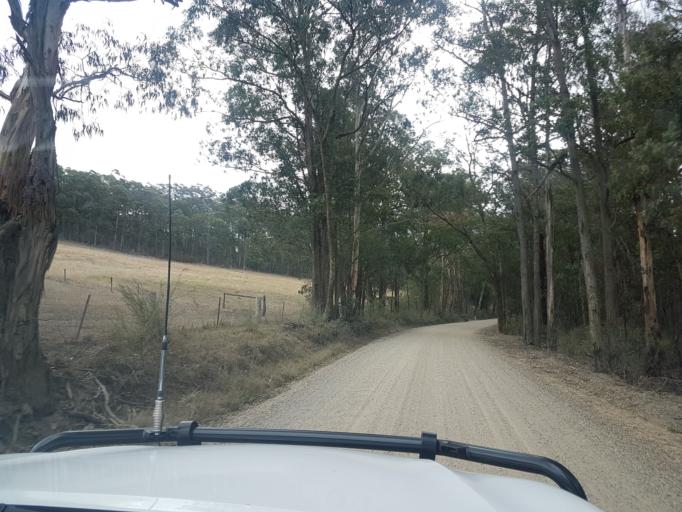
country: AU
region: Victoria
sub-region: East Gippsland
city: Bairnsdale
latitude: -37.6857
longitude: 147.5564
